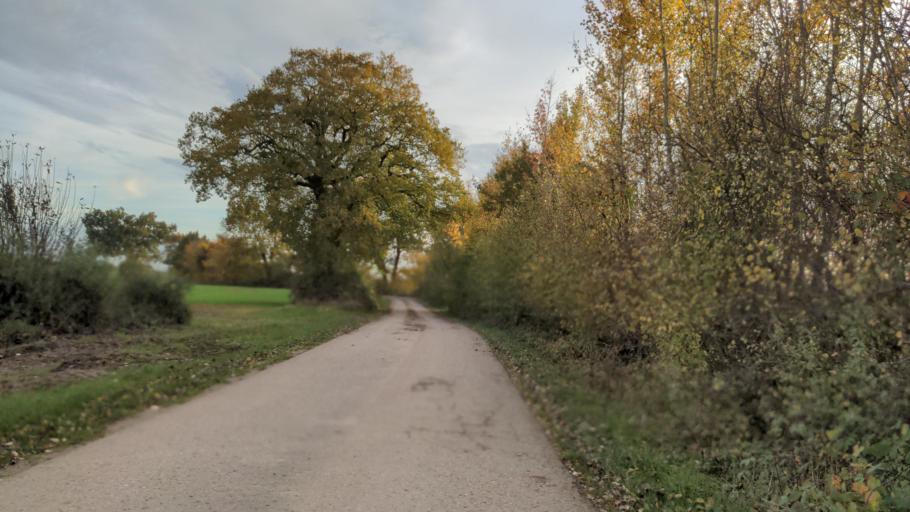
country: DE
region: Schleswig-Holstein
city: Ahrensbok
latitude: 54.0432
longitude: 10.6161
